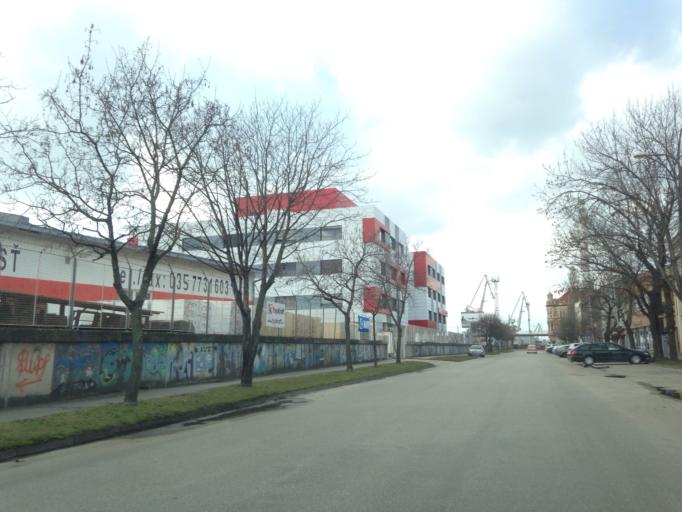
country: SK
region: Nitriansky
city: Komarno
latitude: 47.7559
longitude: 18.1267
